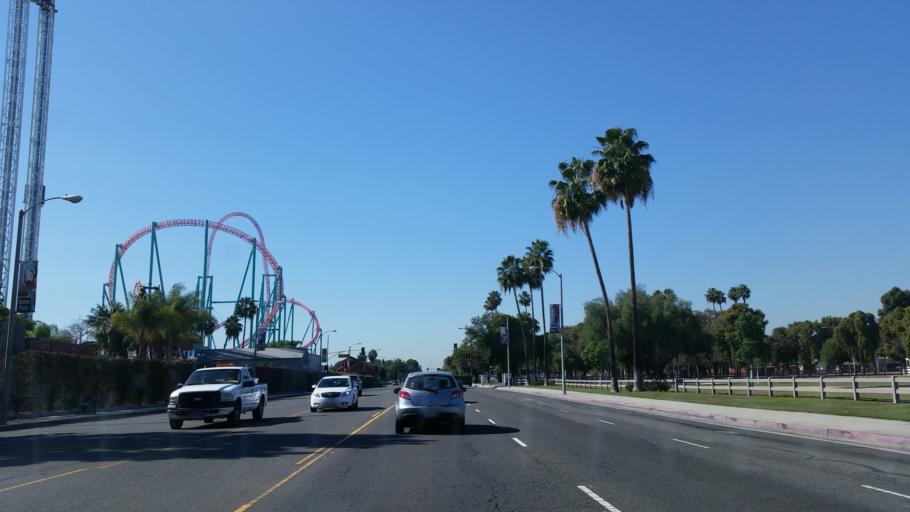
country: US
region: California
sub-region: Orange County
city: Buena Park
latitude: 33.8467
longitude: -117.9990
